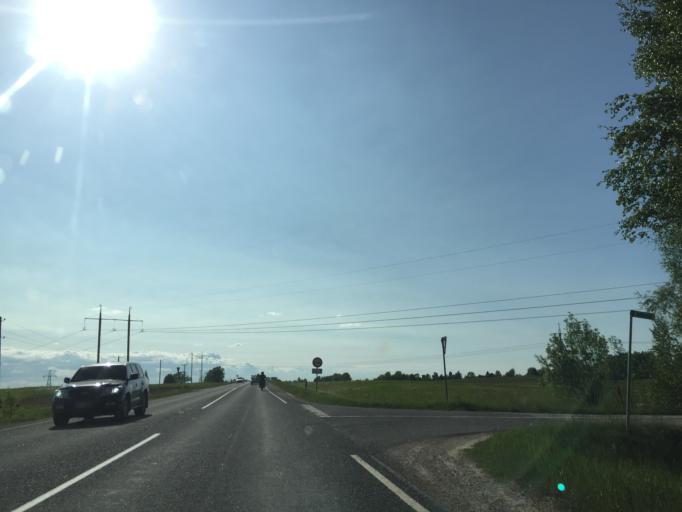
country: LV
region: Salaspils
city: Salaspils
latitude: 56.8261
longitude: 24.3577
